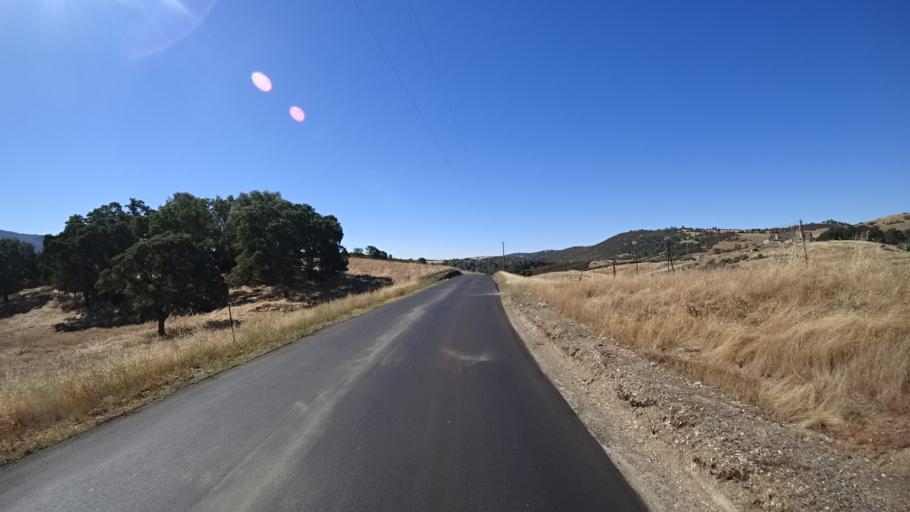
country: US
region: California
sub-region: Calaveras County
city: Rancho Calaveras
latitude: 38.1330
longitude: -120.8134
